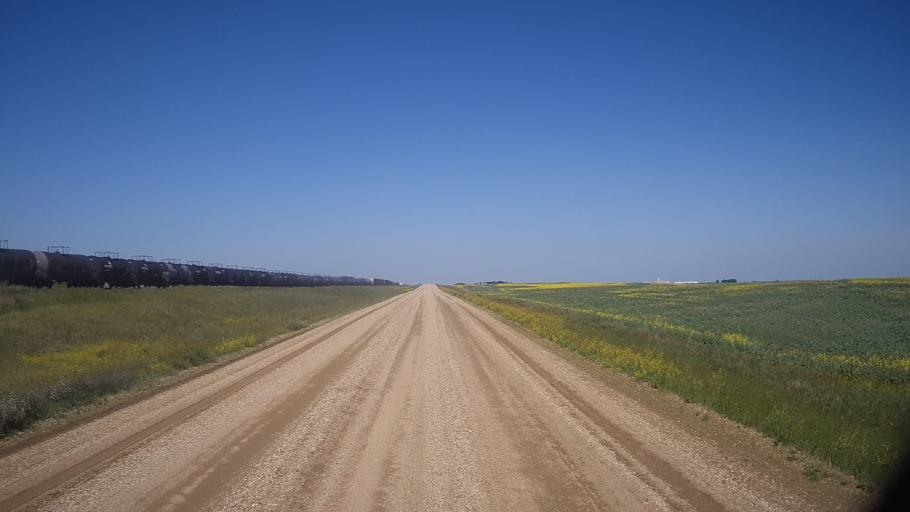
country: CA
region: Saskatchewan
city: Watrous
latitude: 51.8564
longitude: -105.9513
